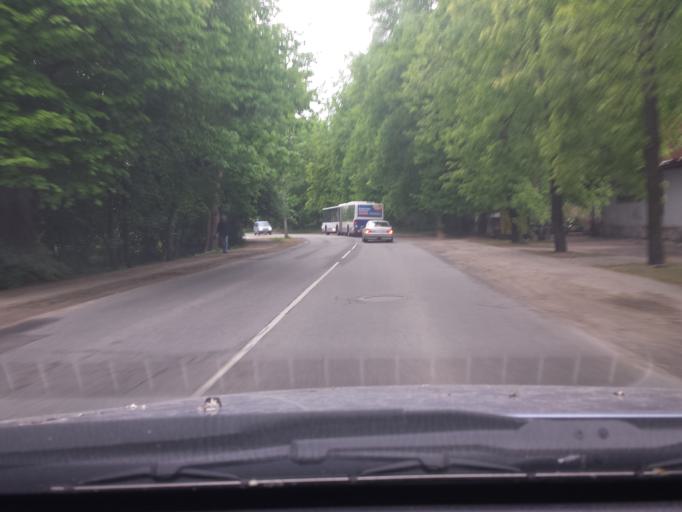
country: LV
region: Marupe
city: Marupe
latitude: 56.9619
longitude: 24.0416
